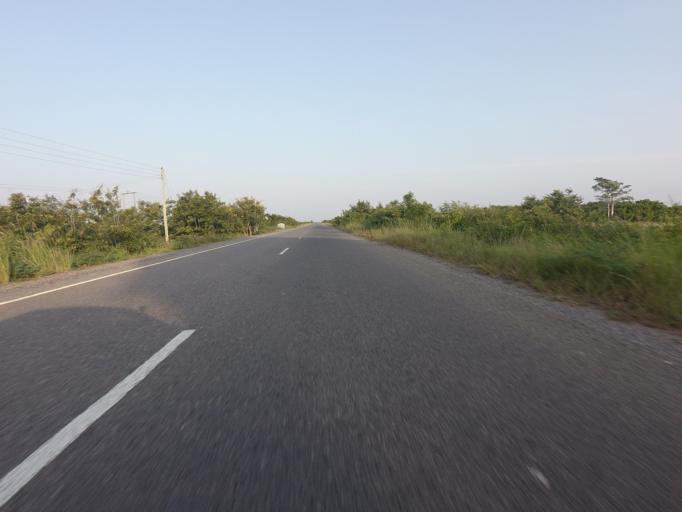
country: GH
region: Volta
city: Anloga
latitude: 5.8874
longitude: 0.7222
